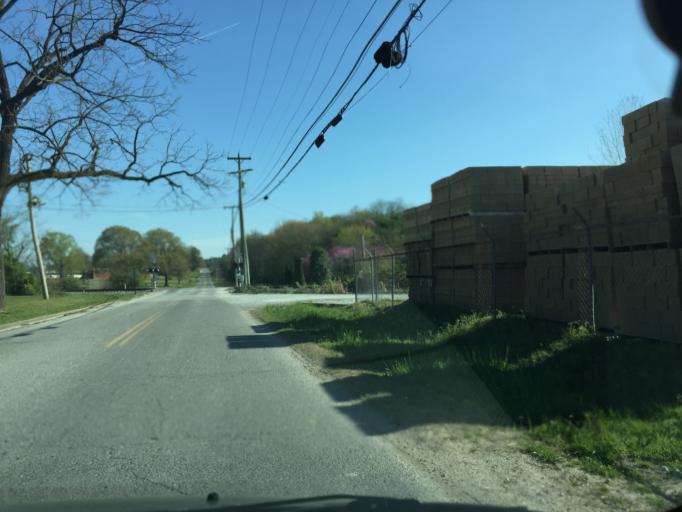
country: US
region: Tennessee
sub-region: Hamilton County
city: East Chattanooga
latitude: 35.0601
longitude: -85.2072
